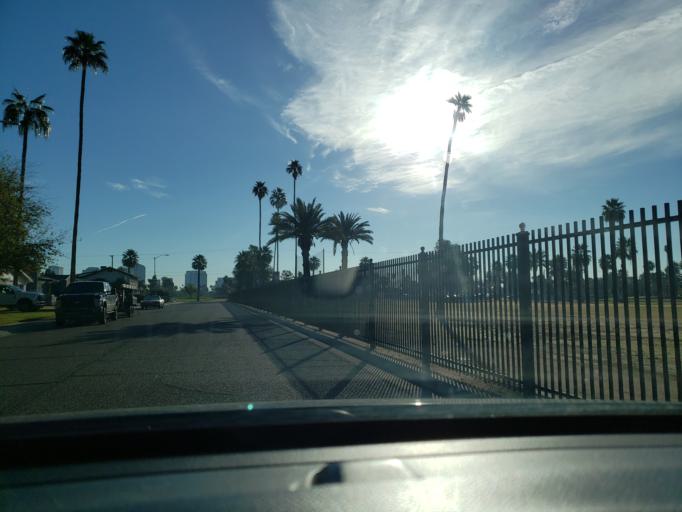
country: US
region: Arizona
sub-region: Maricopa County
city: Phoenix
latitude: 33.4786
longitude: -112.0930
